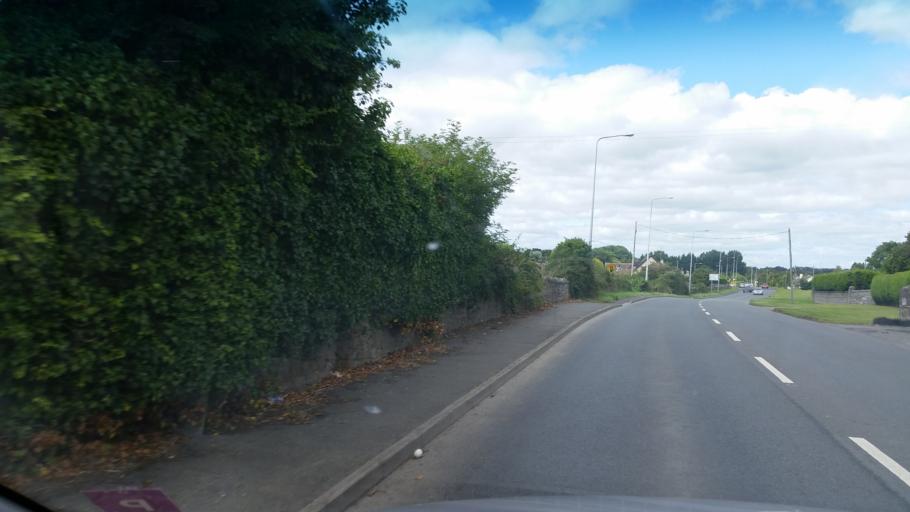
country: IE
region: Leinster
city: Kinsealy-Drinan
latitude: 53.4304
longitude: -6.1776
